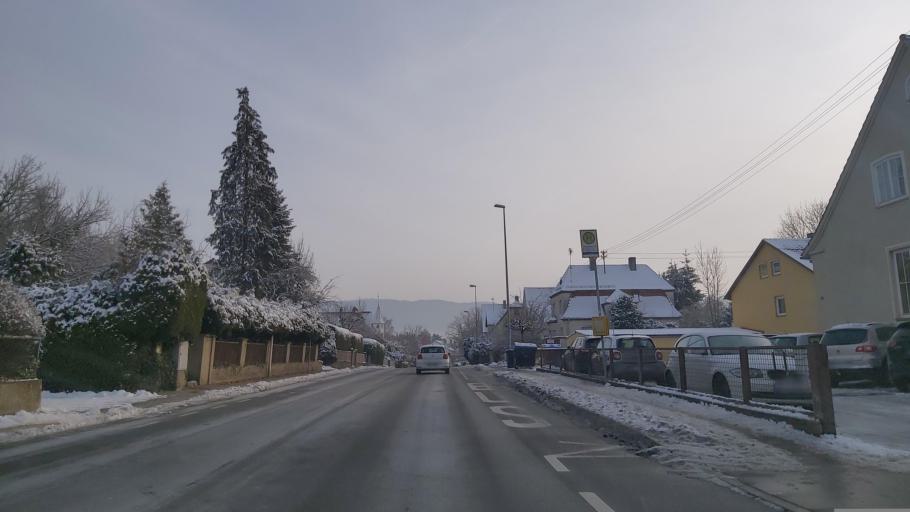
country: DE
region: Baden-Wuerttemberg
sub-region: Tuebingen Region
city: Metzingen
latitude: 48.5459
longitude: 9.2885
